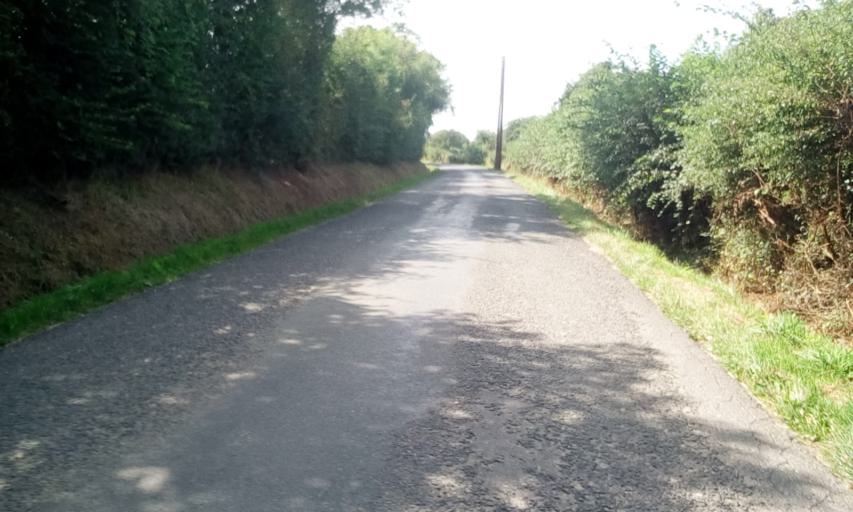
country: FR
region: Lower Normandy
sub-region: Departement du Calvados
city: Argences
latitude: 49.1538
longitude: -0.1430
